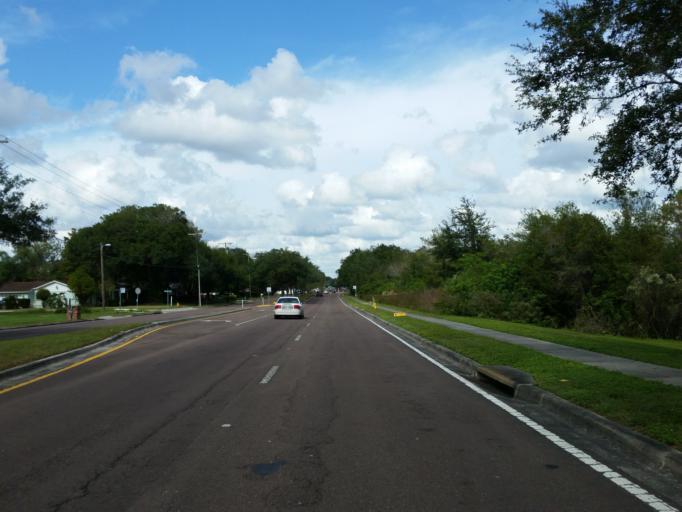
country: US
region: Florida
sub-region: Hillsborough County
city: Brandon
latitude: 27.9168
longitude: -82.2938
